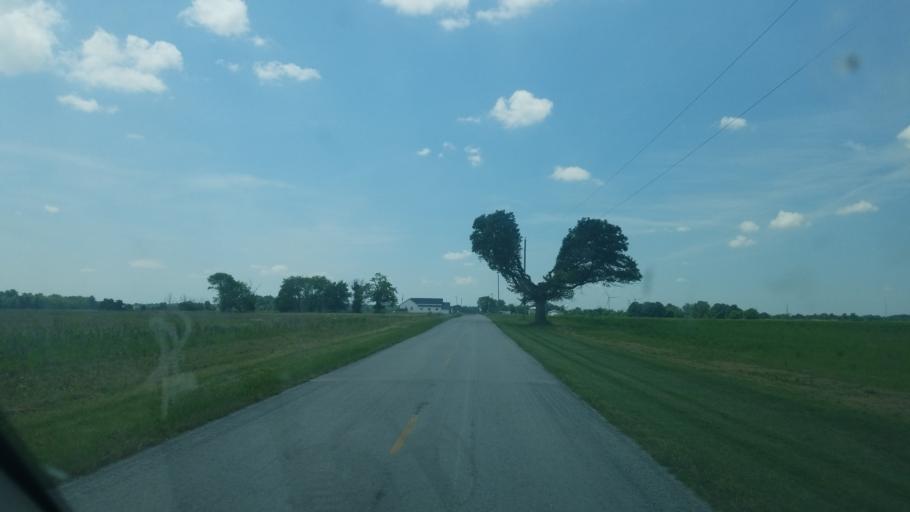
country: US
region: Ohio
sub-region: Hardin County
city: Forest
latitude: 40.7897
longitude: -83.6099
